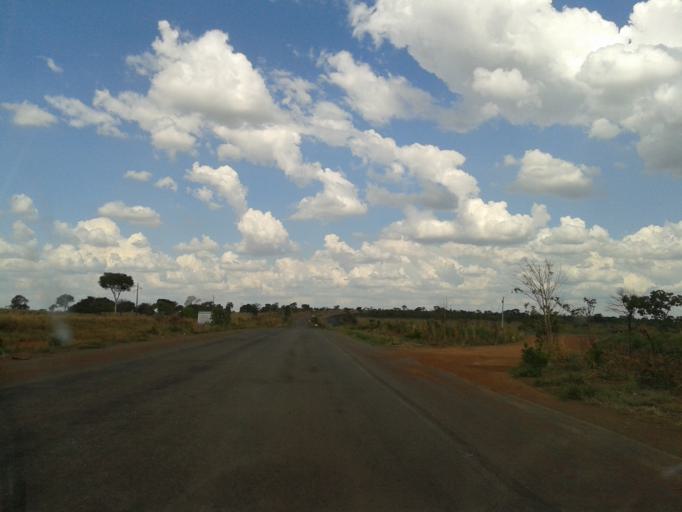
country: BR
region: Goias
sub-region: Caldas Novas
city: Caldas Novas
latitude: -17.6984
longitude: -48.7196
